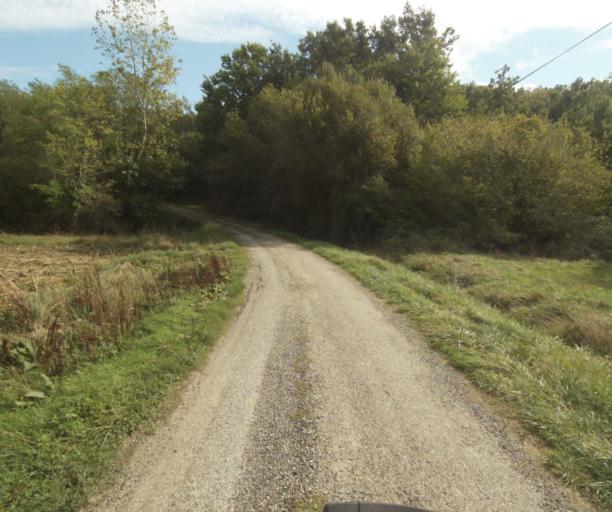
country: FR
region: Midi-Pyrenees
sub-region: Departement du Tarn-et-Garonne
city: Verdun-sur-Garonne
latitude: 43.8659
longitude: 1.1899
